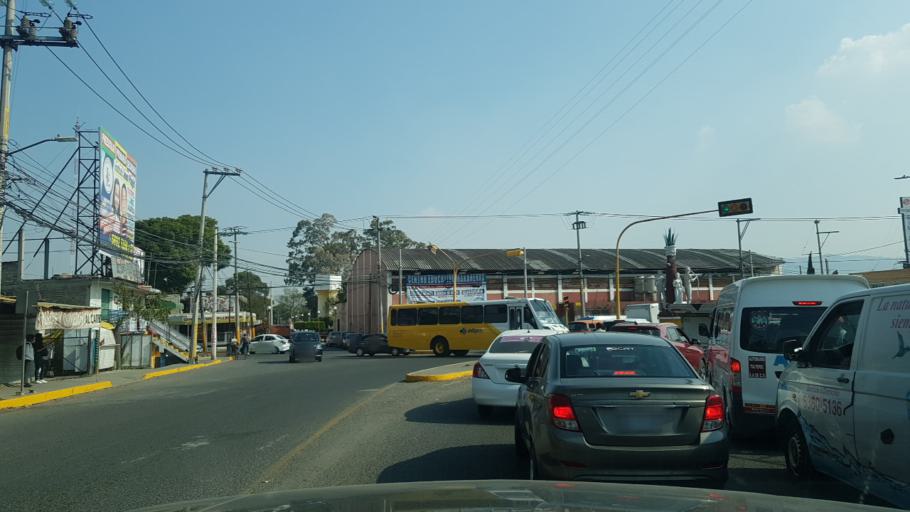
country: MX
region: Mexico
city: Santiago Teyahualco
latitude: 19.6618
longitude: -99.1284
